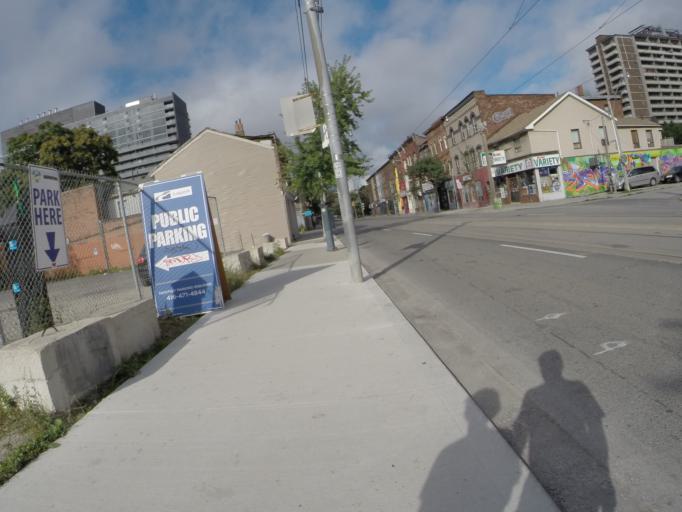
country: CA
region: Ontario
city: Toronto
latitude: 43.6554
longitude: -79.3660
